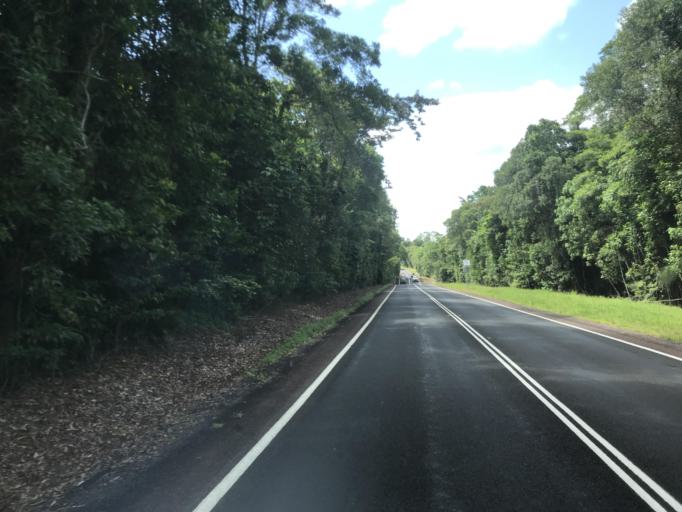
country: AU
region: Queensland
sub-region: Cassowary Coast
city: Innisfail
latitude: -17.8621
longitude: 146.0652
